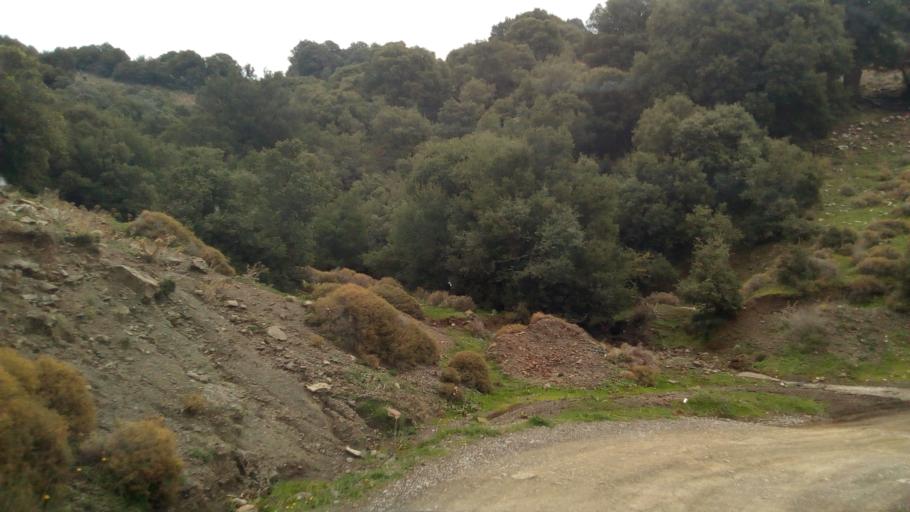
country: GR
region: West Greece
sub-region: Nomos Achaias
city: Selianitika
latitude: 38.4030
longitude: 22.0875
